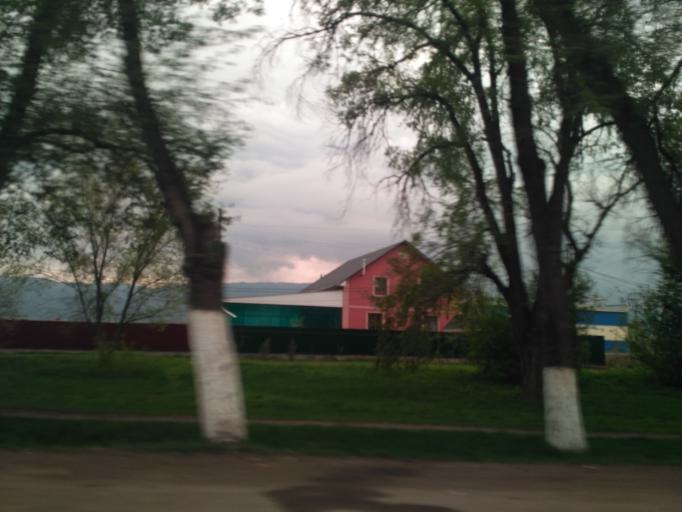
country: KZ
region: Almaty Oblysy
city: Burunday
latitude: 43.2105
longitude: 76.3310
